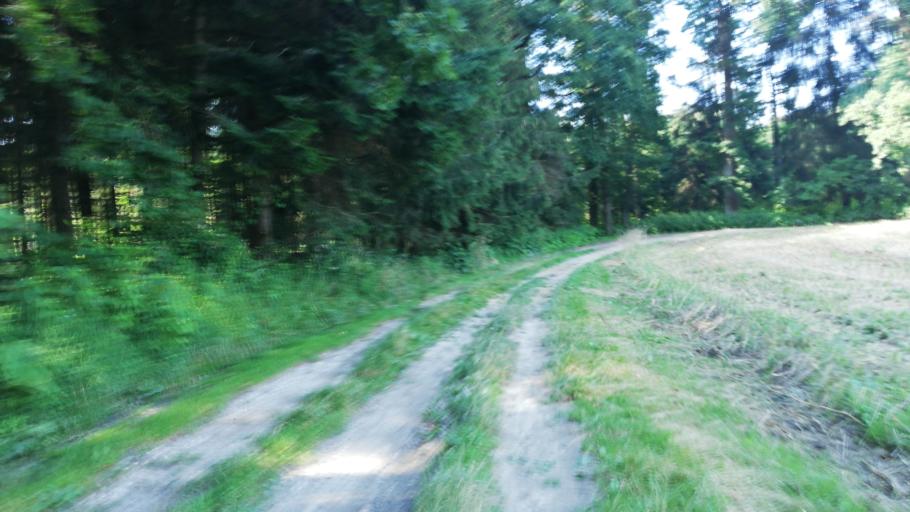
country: AT
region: Upper Austria
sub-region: Wels-Land
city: Gunskirchen
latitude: 48.1673
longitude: 13.9240
